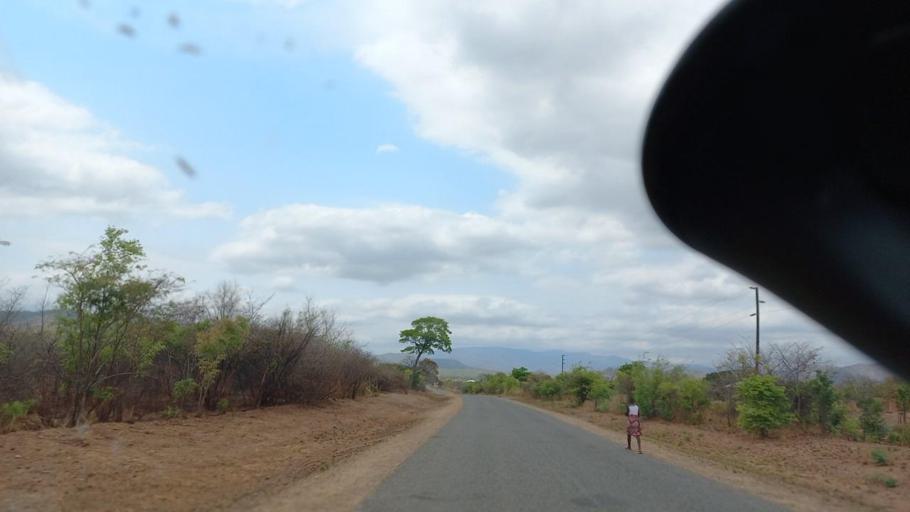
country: ZM
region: Lusaka
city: Luangwa
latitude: -15.0871
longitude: 29.7242
